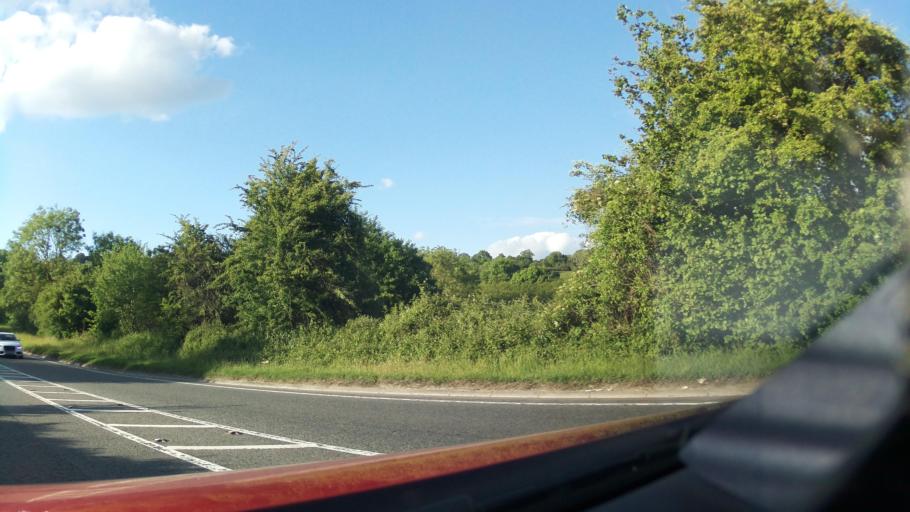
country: GB
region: England
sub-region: Bath and North East Somerset
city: Publow
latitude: 51.3873
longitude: -2.5506
